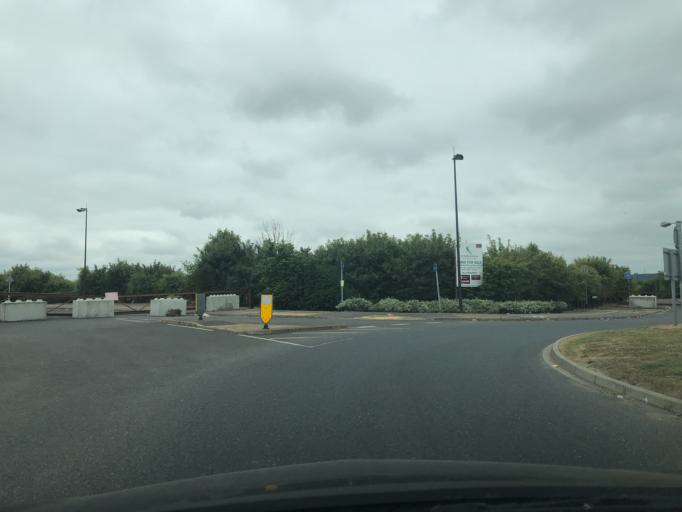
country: GB
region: England
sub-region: North Yorkshire
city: Scarborough
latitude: 54.2329
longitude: -0.4094
